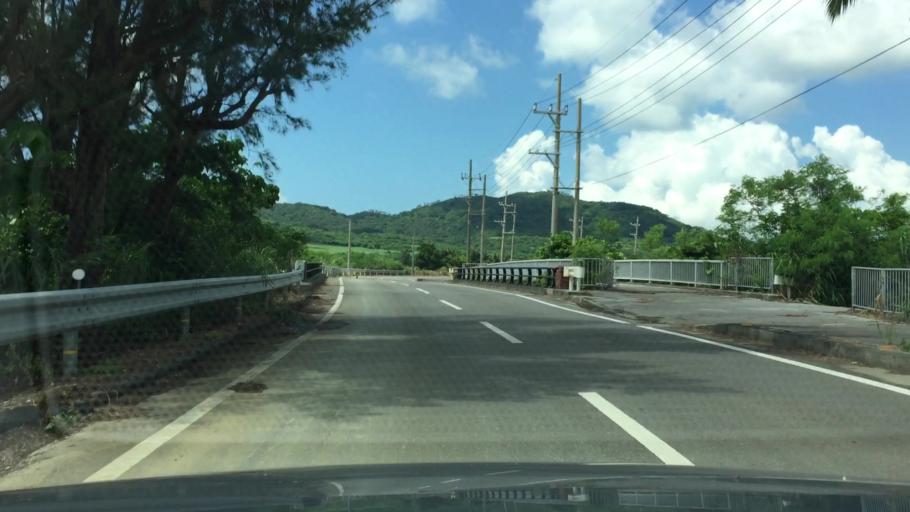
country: JP
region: Okinawa
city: Ishigaki
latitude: 24.3914
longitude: 124.1509
